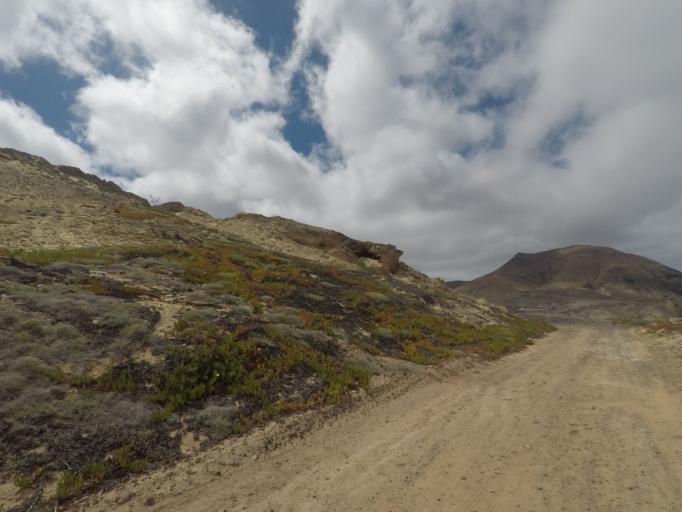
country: PT
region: Madeira
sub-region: Porto Santo
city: Vila de Porto Santo
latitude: 33.0633
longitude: -16.2954
